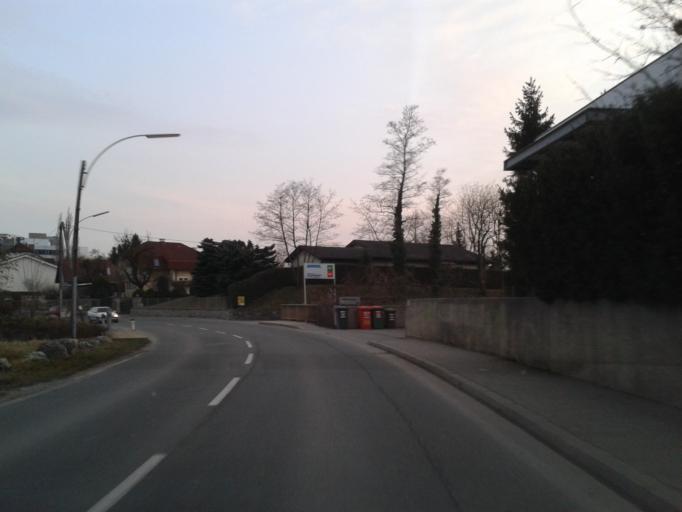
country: AT
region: Styria
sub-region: Politischer Bezirk Graz-Umgebung
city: Stattegg
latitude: 47.1114
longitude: 15.4224
